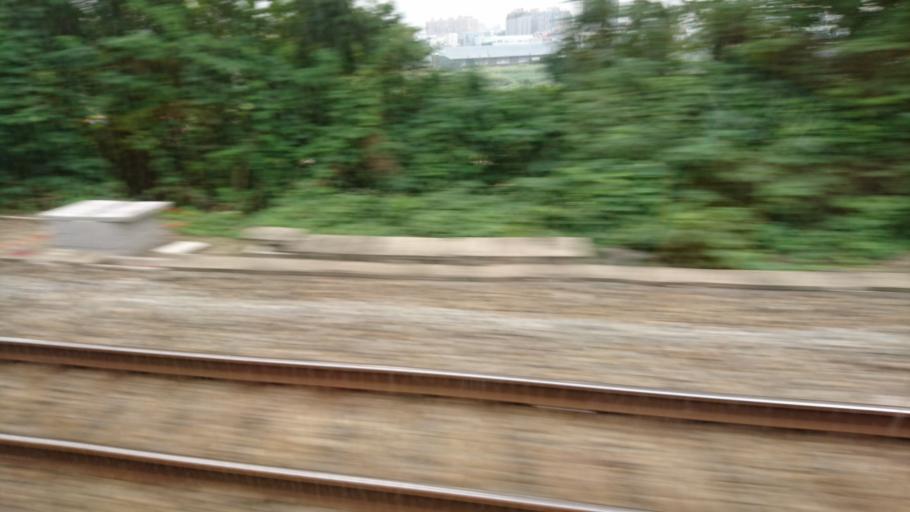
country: TW
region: Taiwan
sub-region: Hsinchu
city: Zhubei
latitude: 24.8552
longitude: 121.0072
